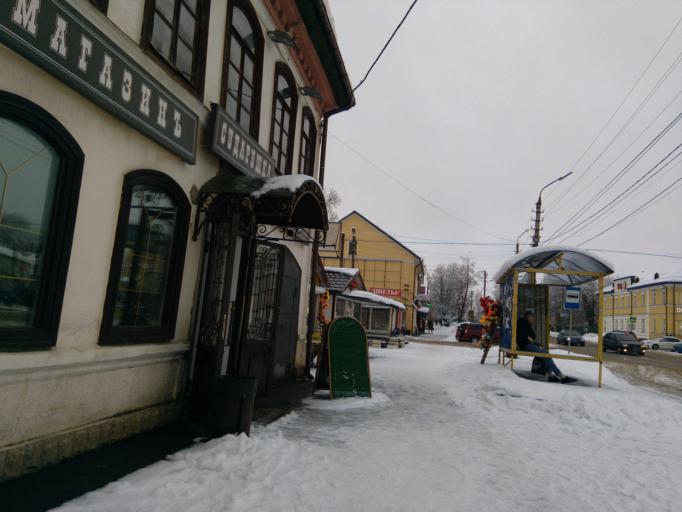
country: RU
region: Tverskaya
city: Torzhok
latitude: 57.0439
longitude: 34.9689
